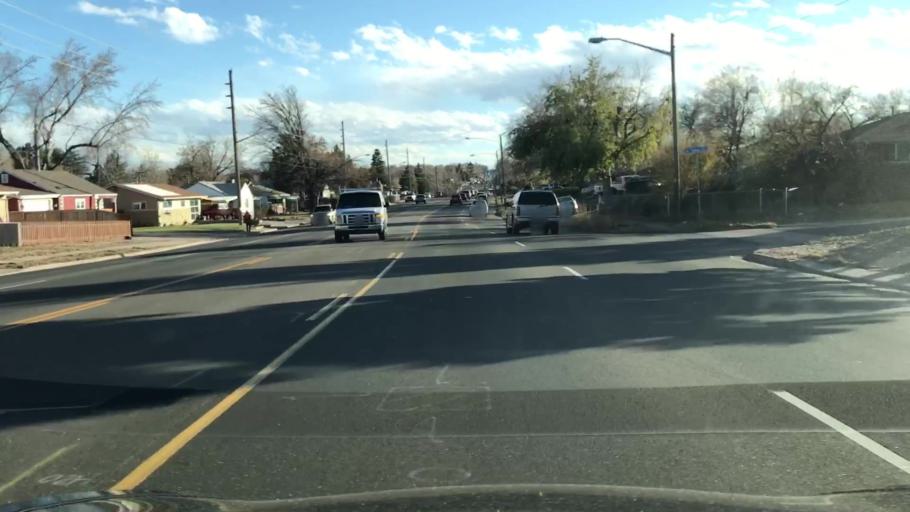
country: US
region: Colorado
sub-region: Jefferson County
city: Lakewood
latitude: 39.6879
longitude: -105.0533
